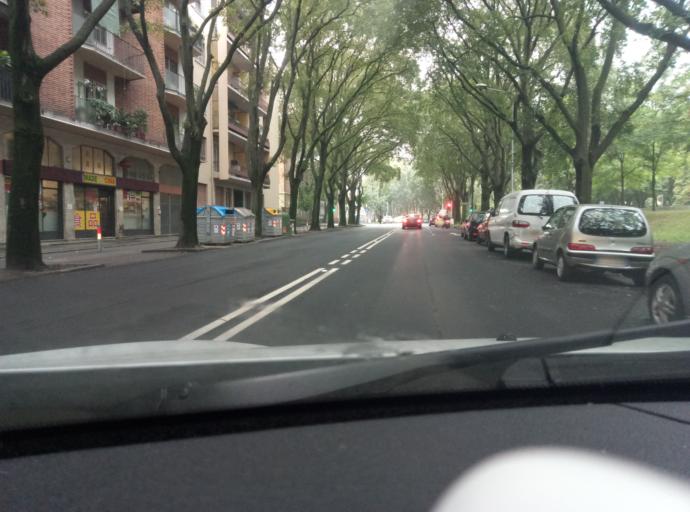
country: IT
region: Emilia-Romagna
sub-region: Provincia di Ferrara
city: Ferrara
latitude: 44.8411
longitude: 11.6064
